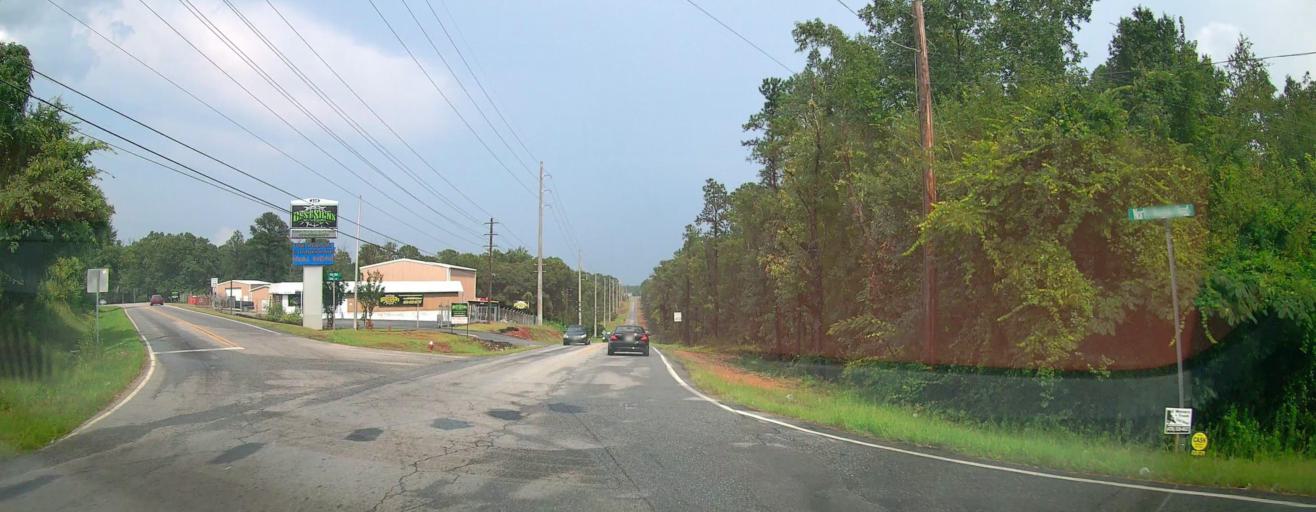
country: US
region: Georgia
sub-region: Houston County
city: Warner Robins
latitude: 32.6509
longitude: -83.6412
